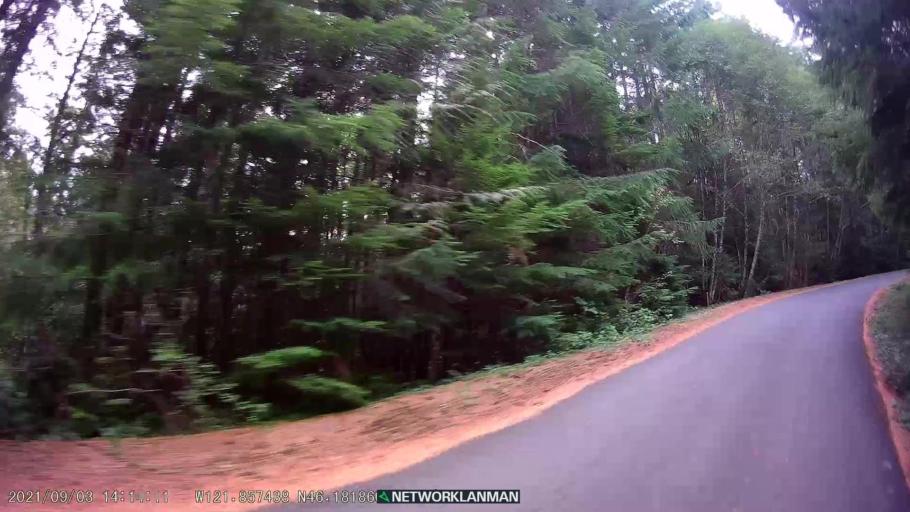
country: US
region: Washington
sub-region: Skamania County
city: Carson
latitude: 46.1818
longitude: -121.8576
